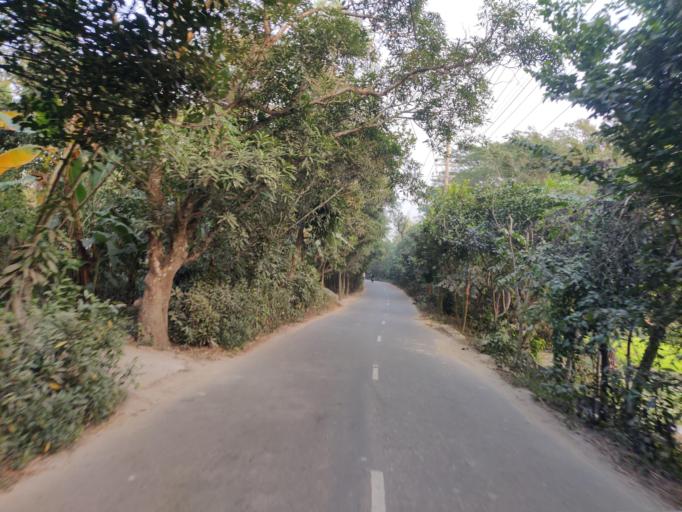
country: BD
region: Dhaka
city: Bajitpur
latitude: 24.1578
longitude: 90.7649
